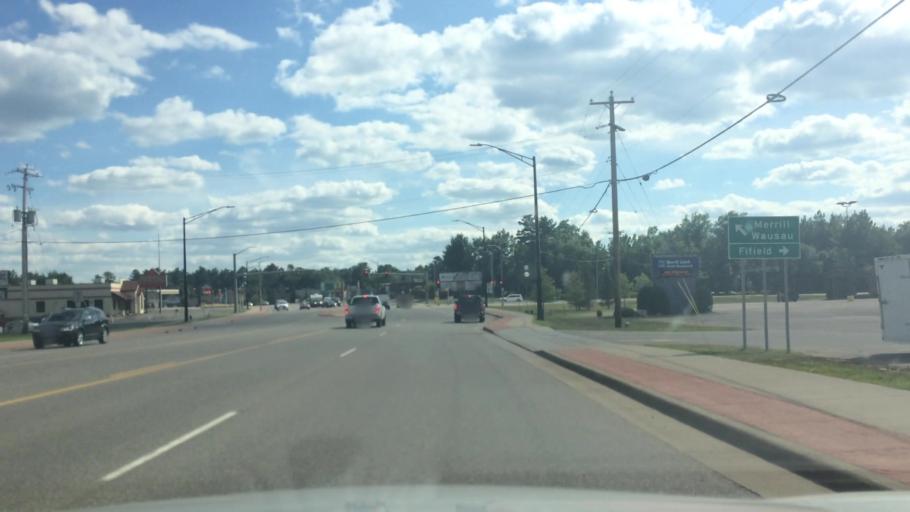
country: US
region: Wisconsin
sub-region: Vilas County
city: Lac du Flambeau
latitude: 45.8890
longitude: -89.7028
